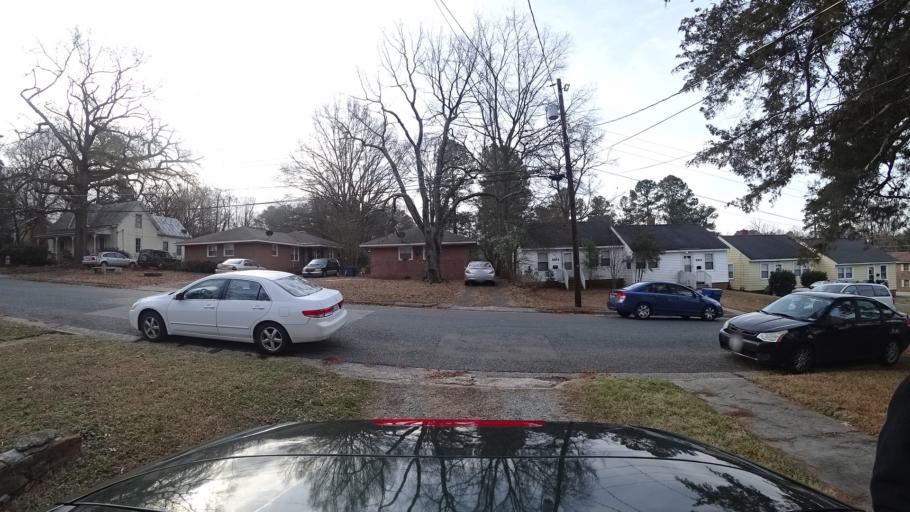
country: US
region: North Carolina
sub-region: Durham County
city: Durham
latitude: 36.0120
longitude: -78.8984
